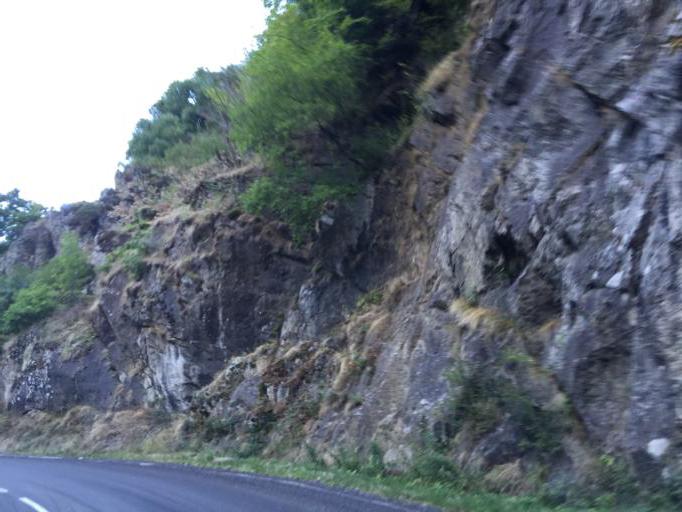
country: FR
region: Auvergne
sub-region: Departement de la Haute-Loire
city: Saugues
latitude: 44.9547
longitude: 3.6307
